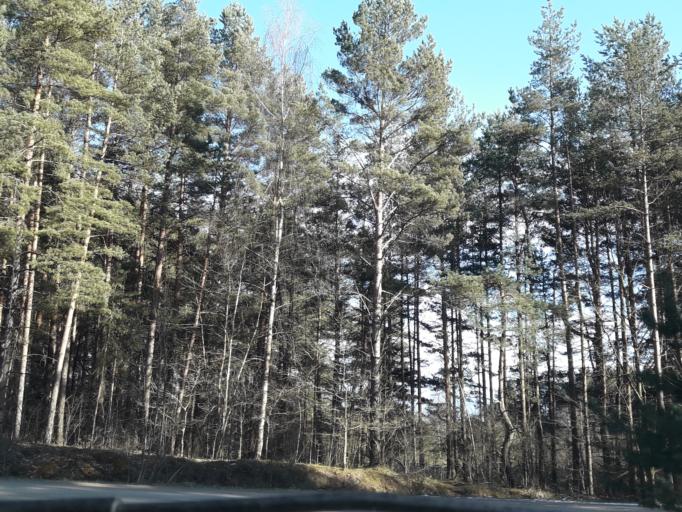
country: LV
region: Kekava
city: Kekava
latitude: 56.8536
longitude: 24.1890
